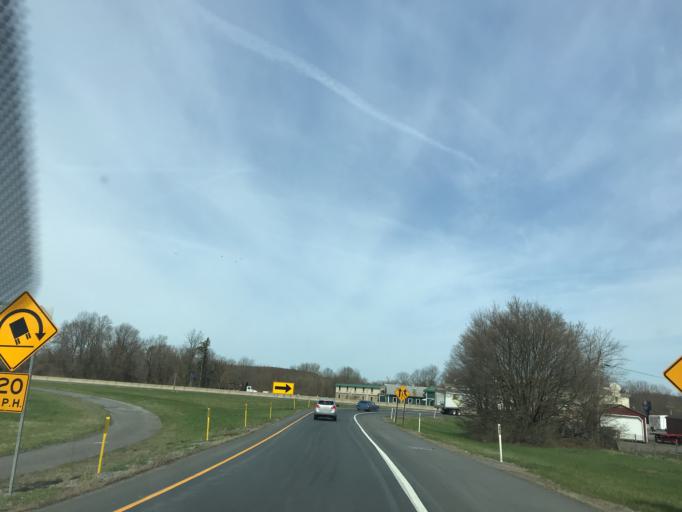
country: US
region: Pennsylvania
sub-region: Snyder County
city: Hummels Wharf
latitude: 40.8189
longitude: -76.8505
